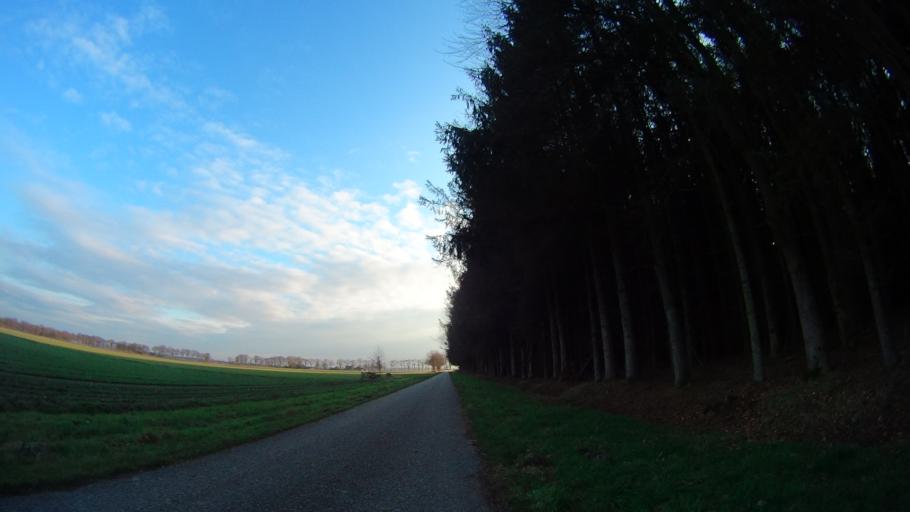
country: NL
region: Drenthe
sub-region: Gemeente Coevorden
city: Sleen
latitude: 52.7971
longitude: 6.7682
